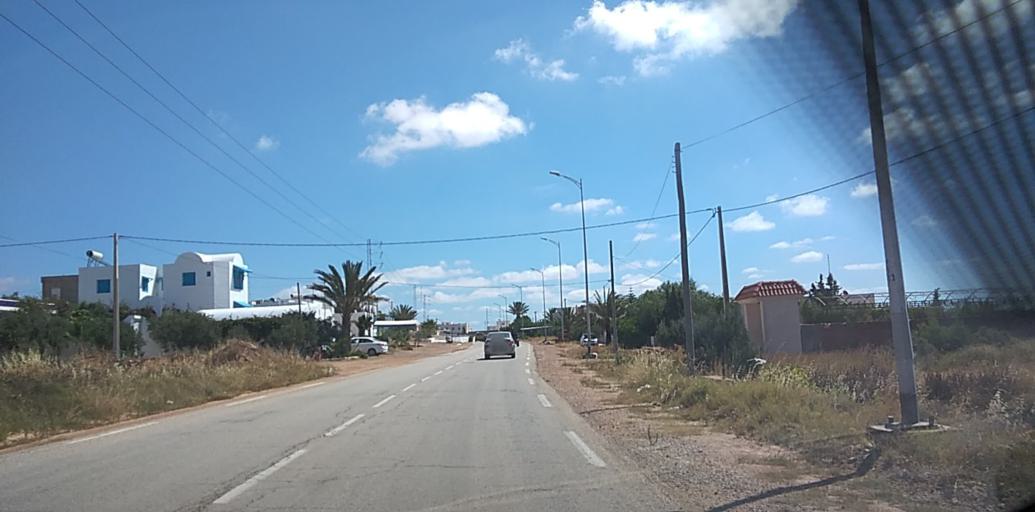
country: TN
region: Safaqis
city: Al Qarmadah
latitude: 34.6751
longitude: 11.1475
